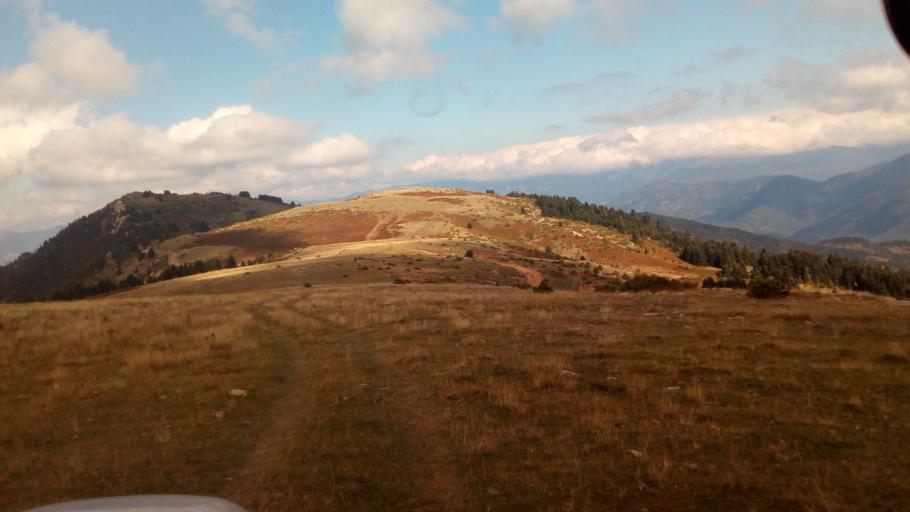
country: GR
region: Central Greece
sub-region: Nomos Fokidos
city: Lidoriki
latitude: 38.6056
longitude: 21.9679
